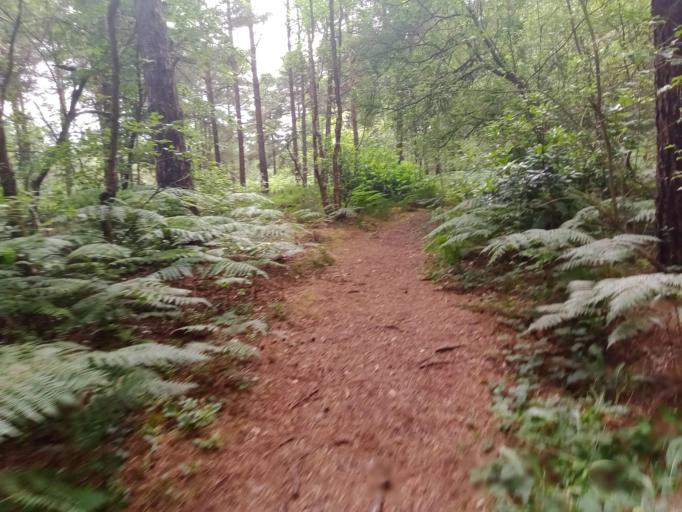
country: IE
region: Leinster
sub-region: Laois
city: Abbeyleix
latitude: 52.8864
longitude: -7.3588
